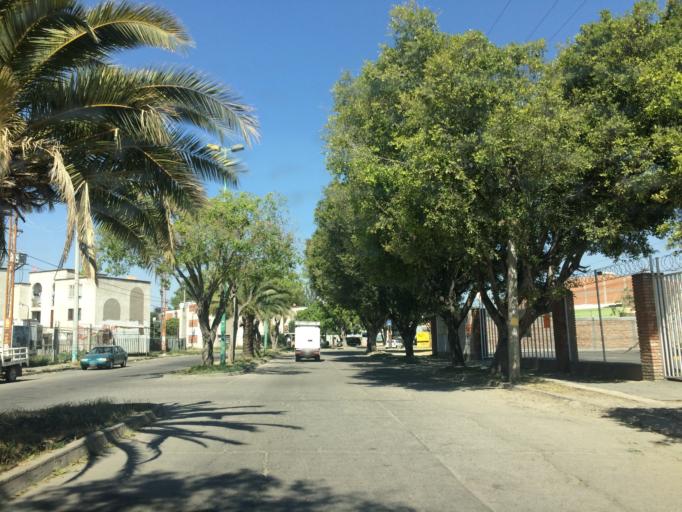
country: MX
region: Guanajuato
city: Leon
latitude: 21.0982
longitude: -101.6706
